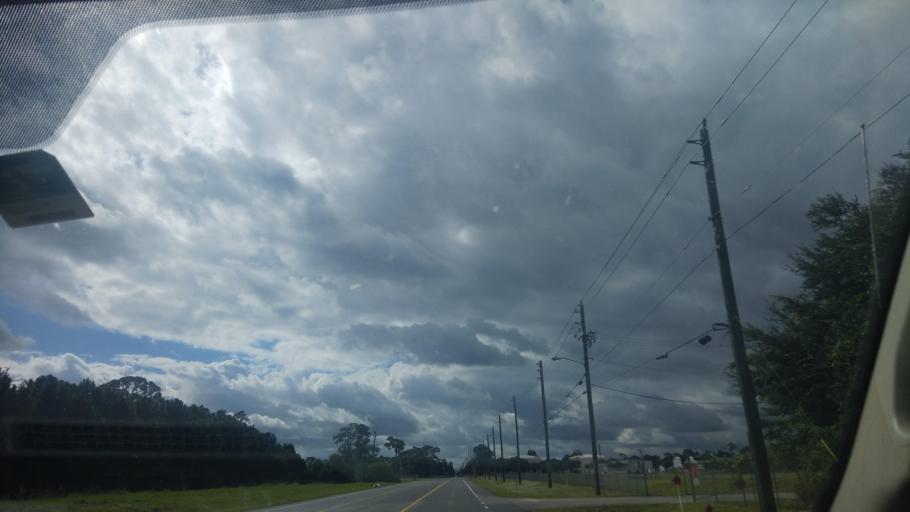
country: US
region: Florida
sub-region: Indian River County
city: Winter Beach
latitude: 27.7395
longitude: -80.4457
